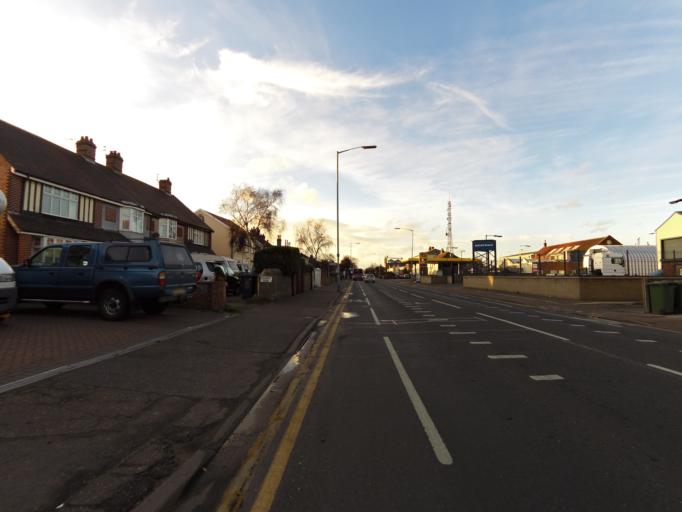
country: GB
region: England
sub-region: Norfolk
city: Great Yarmouth
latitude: 52.6010
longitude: 1.7231
